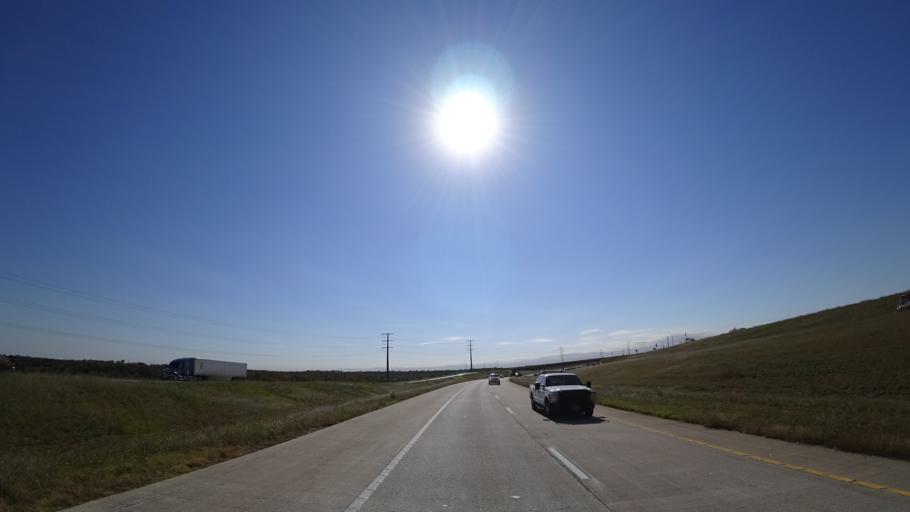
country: US
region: Texas
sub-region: Travis County
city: Garfield
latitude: 30.1207
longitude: -97.6598
